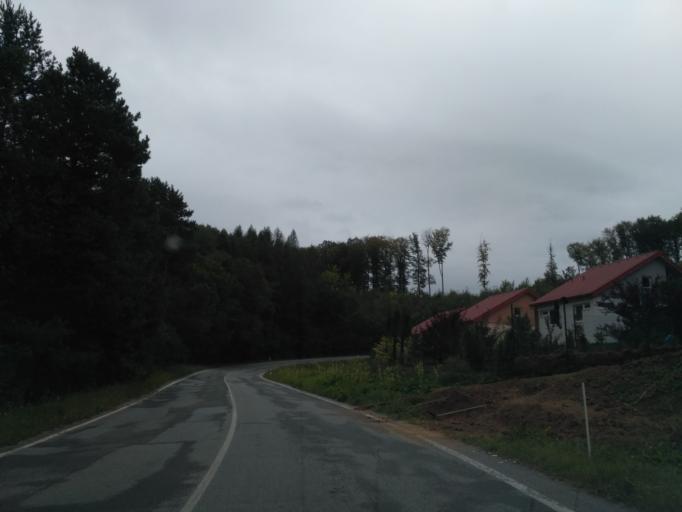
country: SK
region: Presovsky
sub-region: Okres Presov
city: Presov
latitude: 48.9875
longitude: 21.1881
